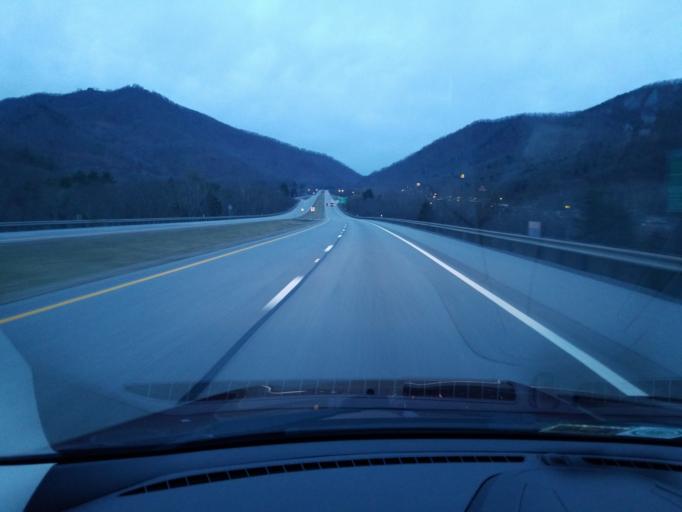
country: US
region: West Virginia
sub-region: Greenbrier County
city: White Sulphur Springs
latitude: 37.7712
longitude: -80.3462
